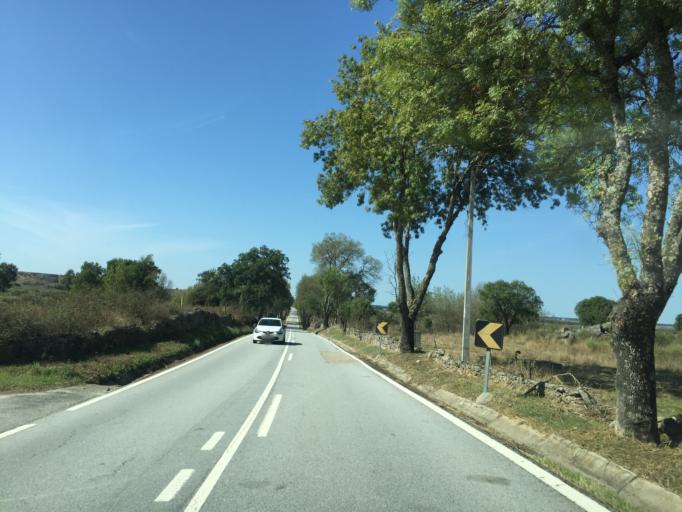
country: PT
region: Portalegre
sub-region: Portalegre
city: Alagoa
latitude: 39.4394
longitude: -7.5615
